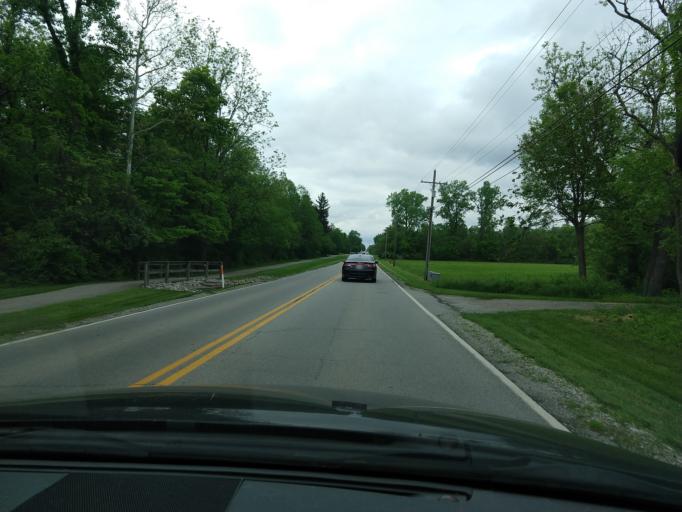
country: US
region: Indiana
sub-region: Hamilton County
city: Westfield
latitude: 40.0242
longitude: -86.1275
